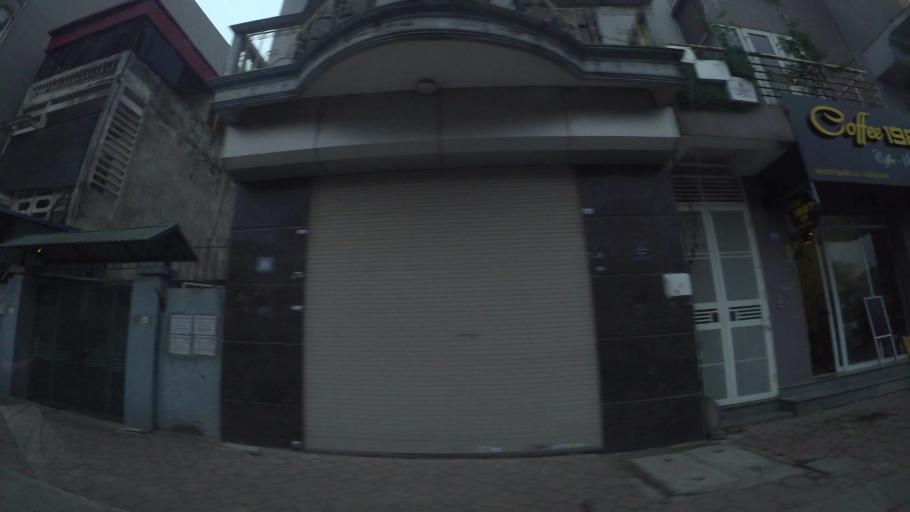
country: VN
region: Ha Noi
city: Hai BaTrung
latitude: 20.9935
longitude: 105.8364
